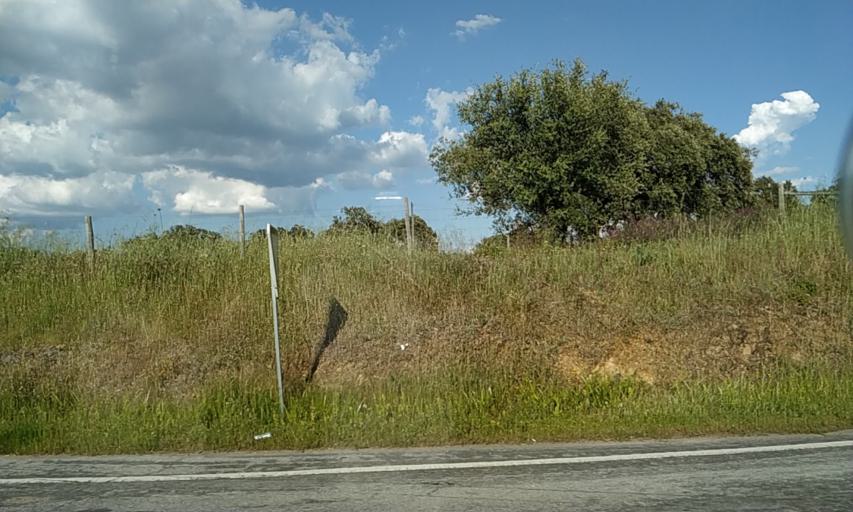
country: PT
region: Portalegre
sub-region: Portalegre
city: Urra
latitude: 39.1686
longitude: -7.4538
